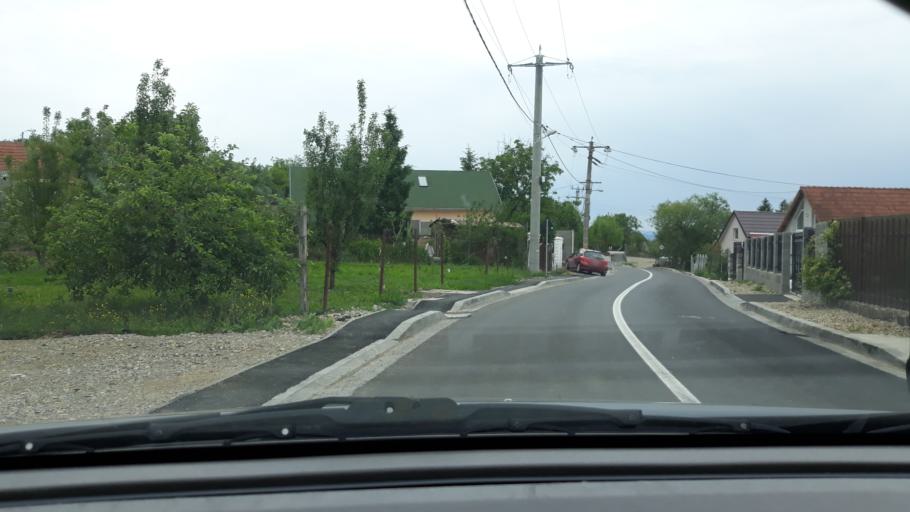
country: RO
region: Bihor
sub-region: Comuna Osorheiu
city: Osorheiu
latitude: 47.0592
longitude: 22.0167
